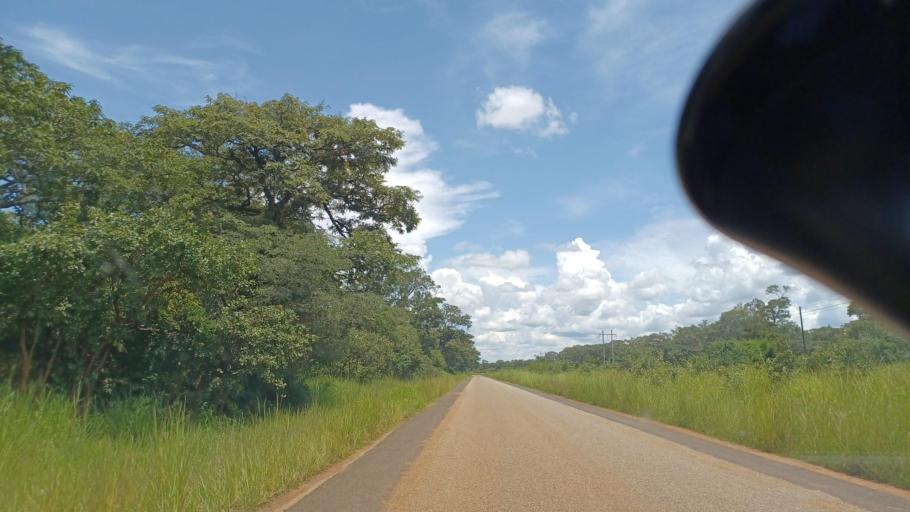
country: ZM
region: North-Western
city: Solwezi
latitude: -12.5751
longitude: 26.1333
